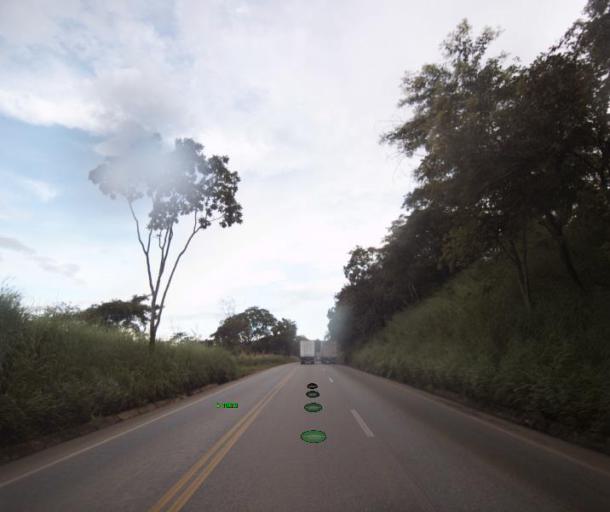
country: BR
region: Goias
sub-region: Porangatu
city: Porangatu
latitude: -13.9700
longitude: -49.0904
